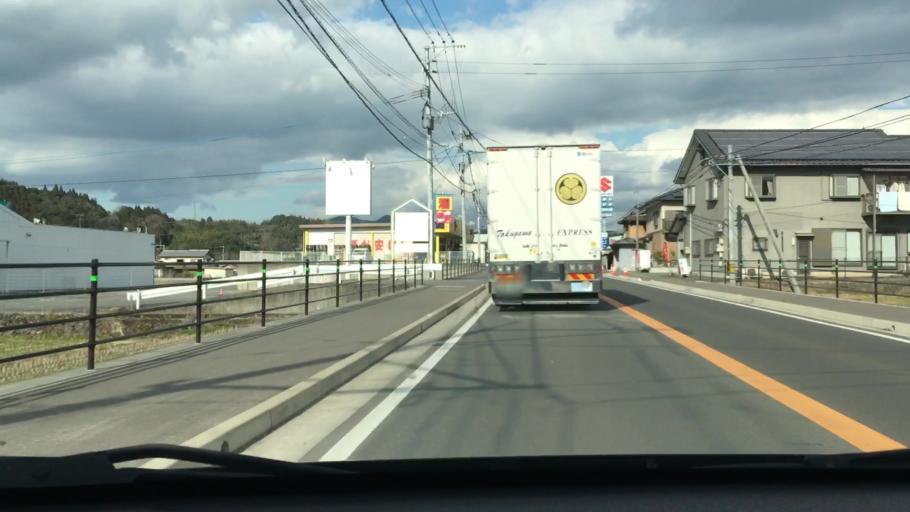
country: JP
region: Oita
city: Usuki
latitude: 33.0344
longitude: 131.6892
